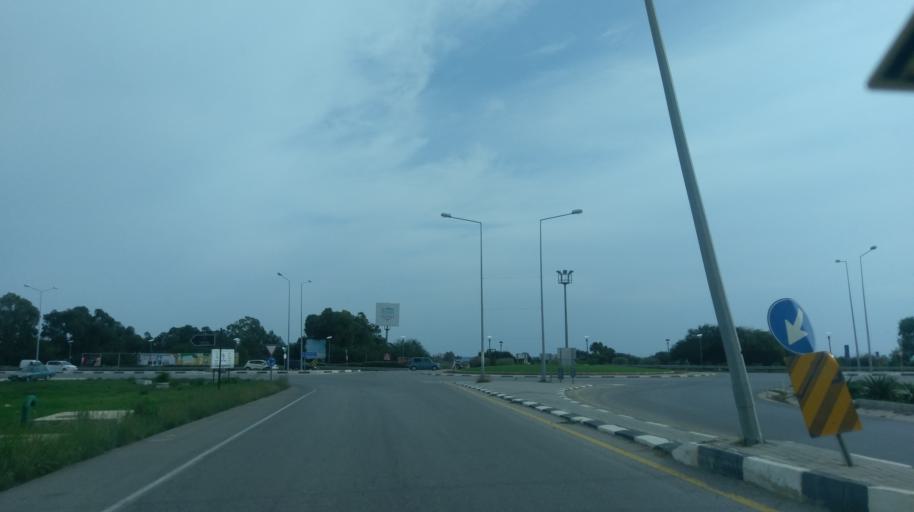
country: CY
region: Ammochostos
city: Trikomo
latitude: 35.2790
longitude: 33.9196
